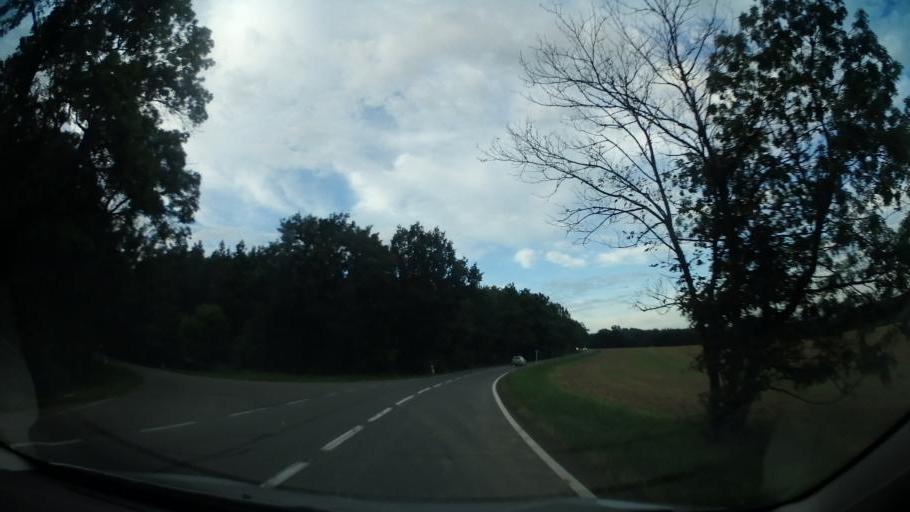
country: CZ
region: Olomoucky
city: Bila Lhota
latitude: 49.6840
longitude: 16.9950
